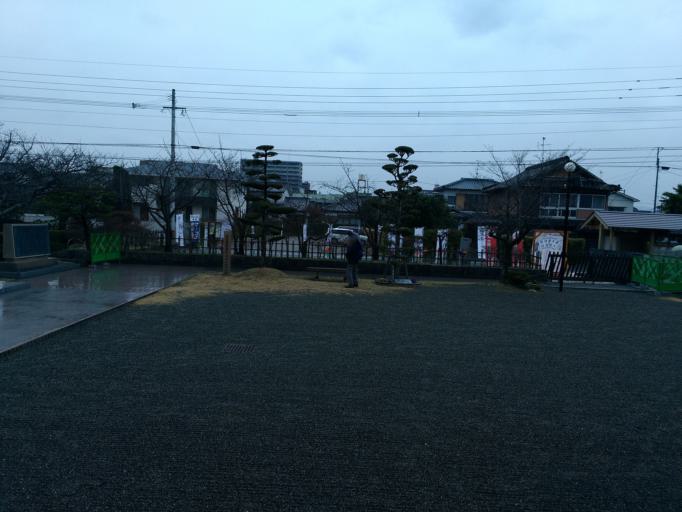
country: JP
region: Saga Prefecture
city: Saga-shi
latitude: 33.2481
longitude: 130.3088
